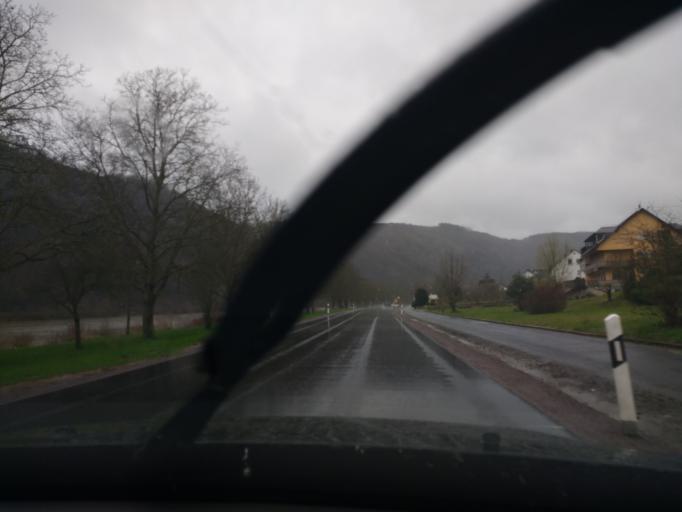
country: DE
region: Rheinland-Pfalz
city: Krov
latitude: 49.9742
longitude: 7.0858
